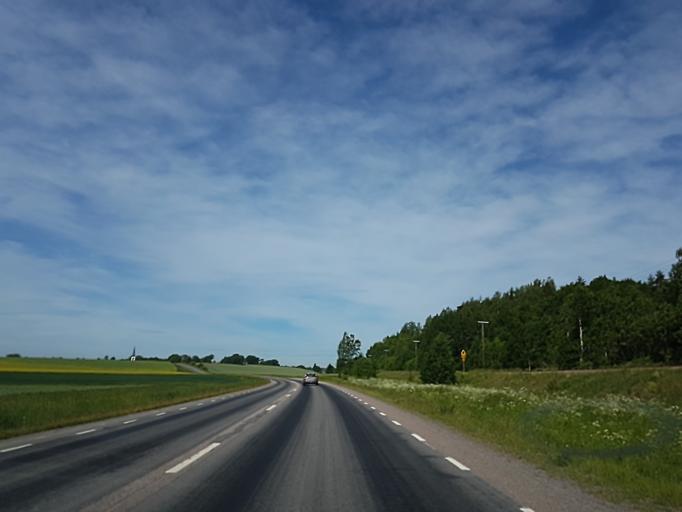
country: SE
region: Soedermanland
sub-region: Nykopings Kommun
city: Stigtomta
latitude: 58.7442
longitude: 16.7623
